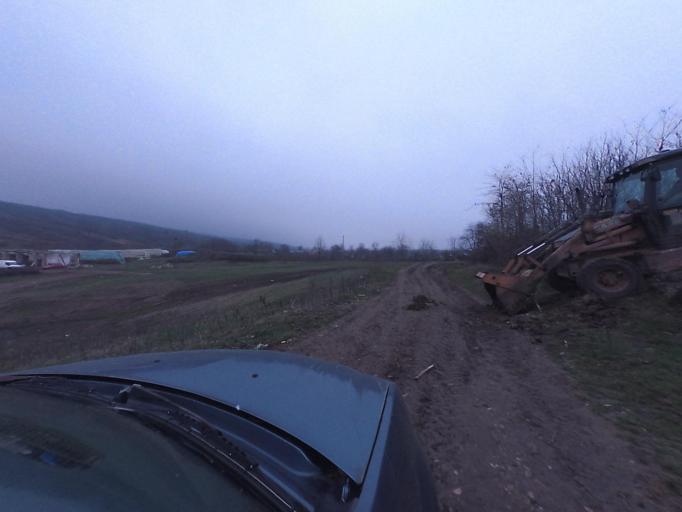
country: RO
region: Galati
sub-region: Comuna Balabanesti
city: Balabanesti
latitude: 46.1351
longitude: 27.7503
